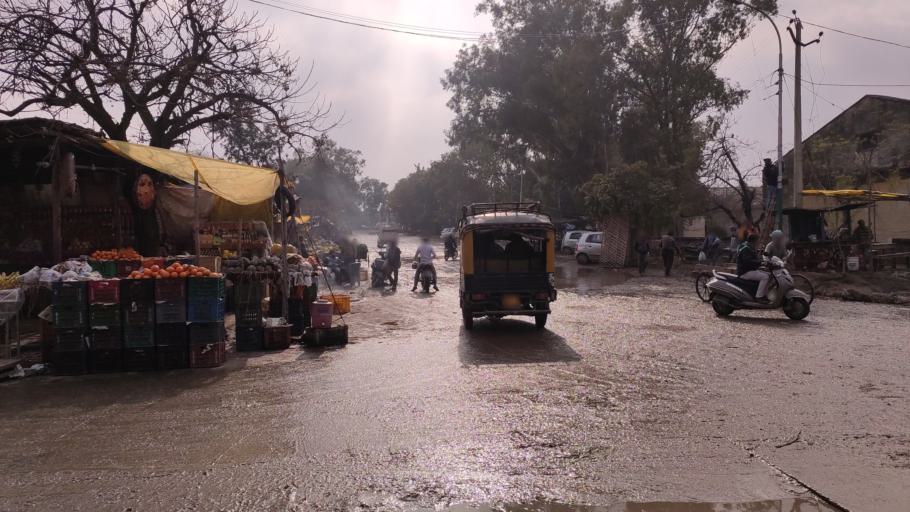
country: IN
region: Punjab
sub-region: Amritsar
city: Amritsar
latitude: 31.6269
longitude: 74.9199
